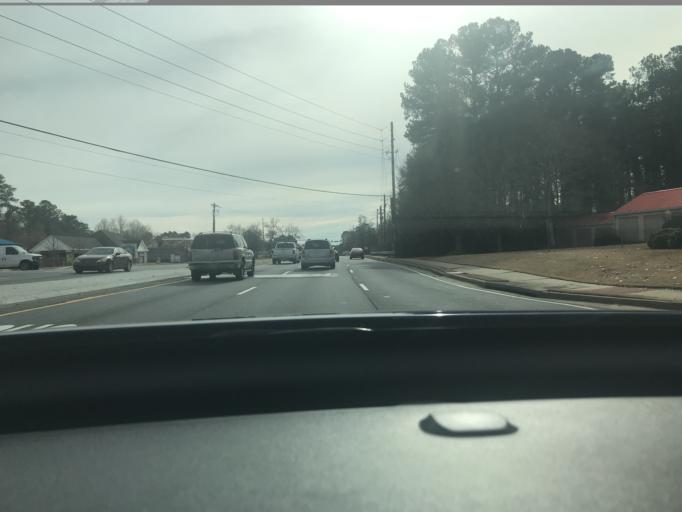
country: US
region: Georgia
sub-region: Gwinnett County
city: Lilburn
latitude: 33.9390
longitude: -84.1212
